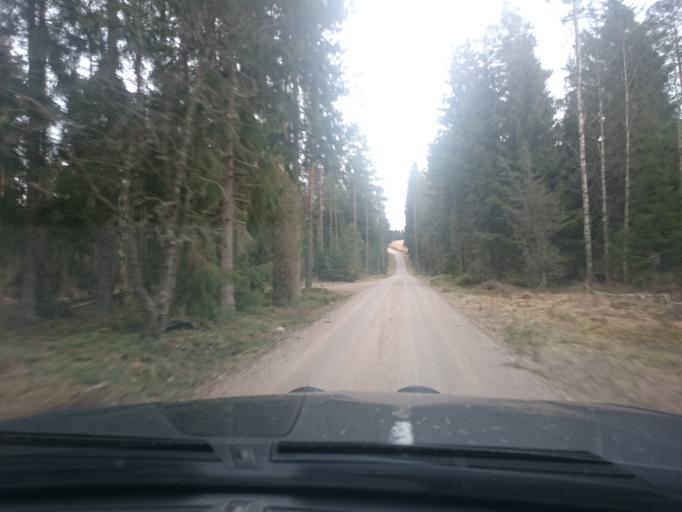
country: SE
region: Joenkoeping
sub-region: Vetlanda Kommun
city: Vetlanda
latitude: 57.2864
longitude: 15.1675
